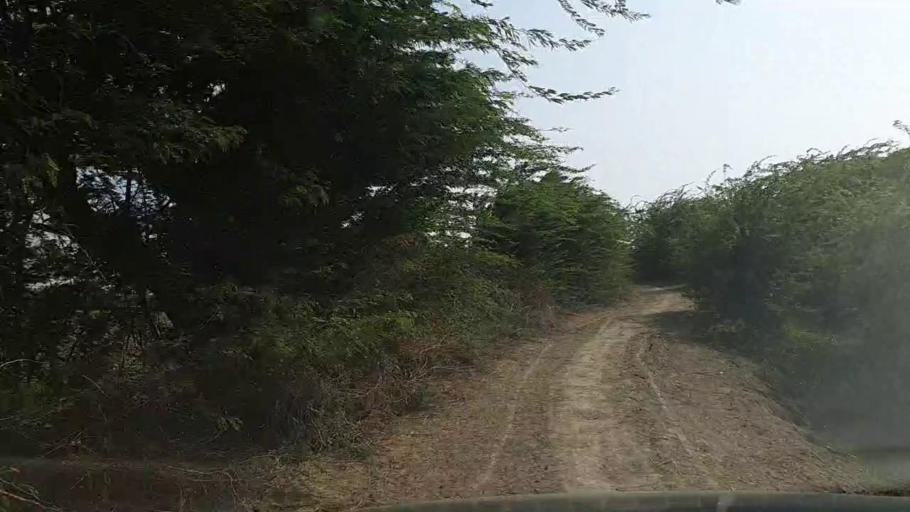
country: PK
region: Sindh
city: Gharo
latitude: 24.7341
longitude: 67.6858
